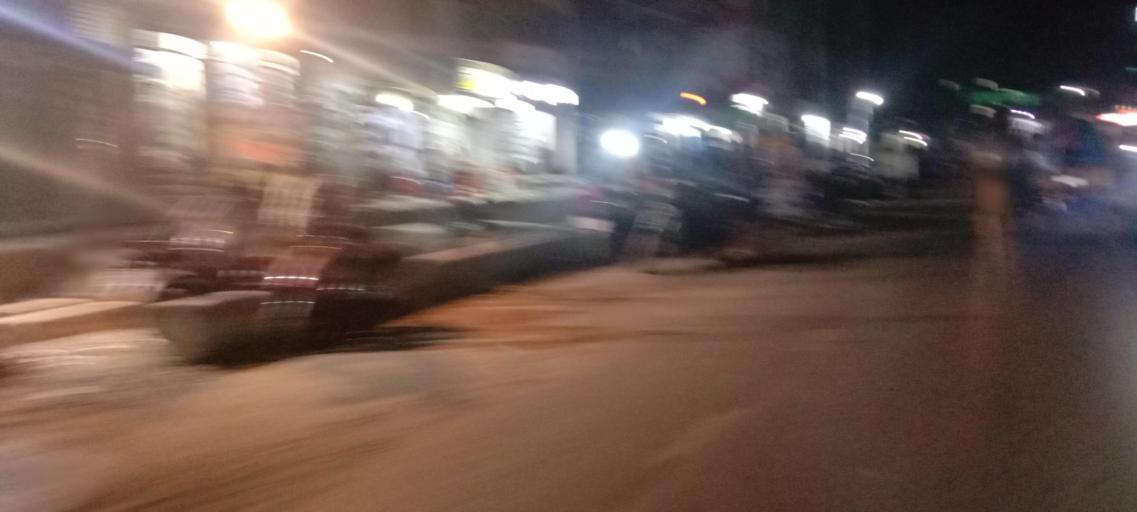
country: BD
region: Dhaka
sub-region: Dhaka
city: Dhaka
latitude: 23.7022
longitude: 90.3908
